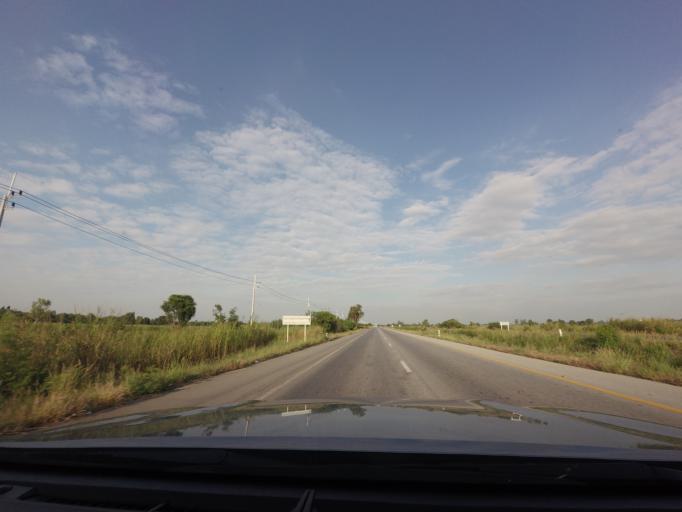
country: TH
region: Nakhon Sawan
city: Nakhon Sawan
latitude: 15.7592
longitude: 100.0942
